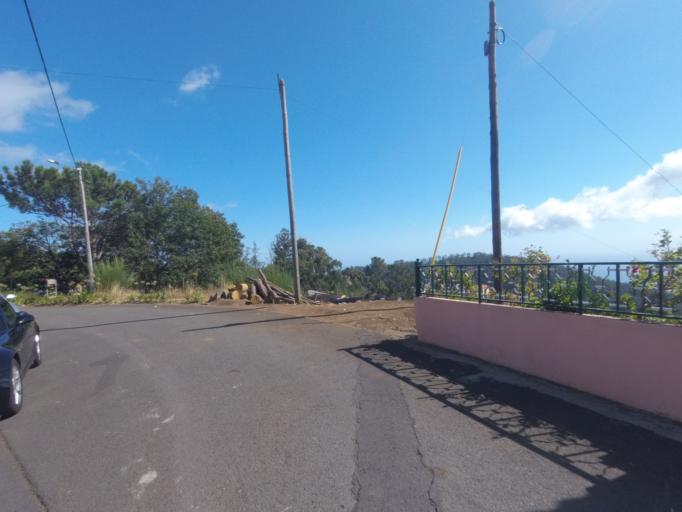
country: PT
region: Madeira
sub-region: Ribeira Brava
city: Campanario
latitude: 32.6975
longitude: -17.0304
